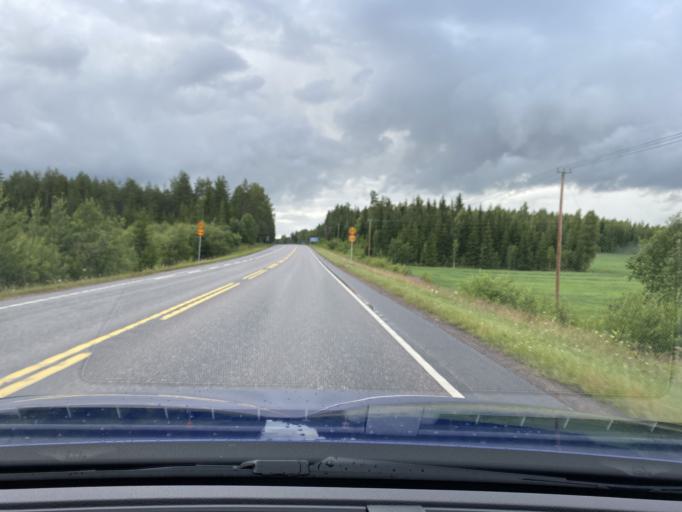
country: FI
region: Uusimaa
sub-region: Helsinki
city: Hyvinge
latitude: 60.5575
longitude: 24.8211
